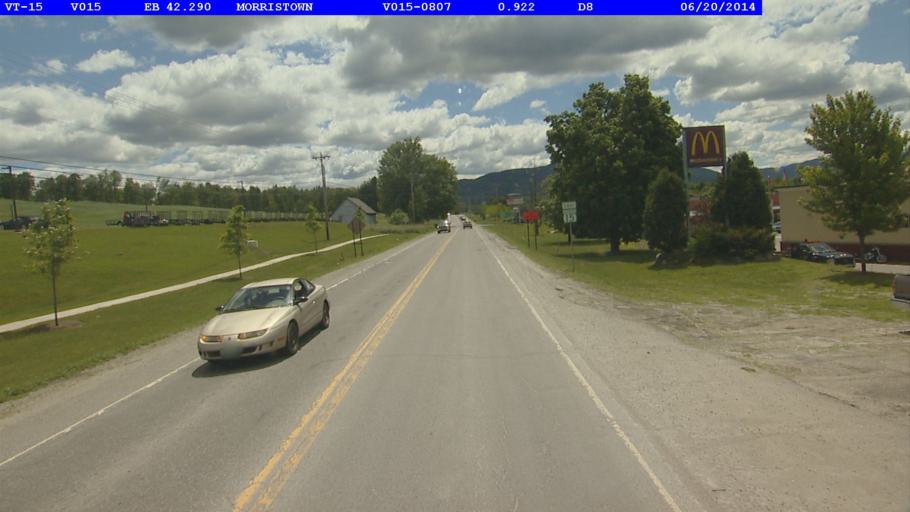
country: US
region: Vermont
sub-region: Lamoille County
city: Morrisville
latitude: 44.5752
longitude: -72.5917
